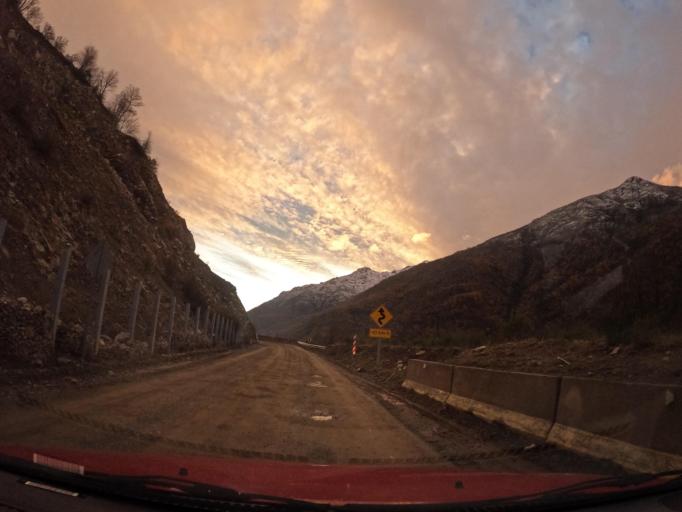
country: CL
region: Maule
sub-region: Provincia de Linares
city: Colbun
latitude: -35.8565
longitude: -71.1663
